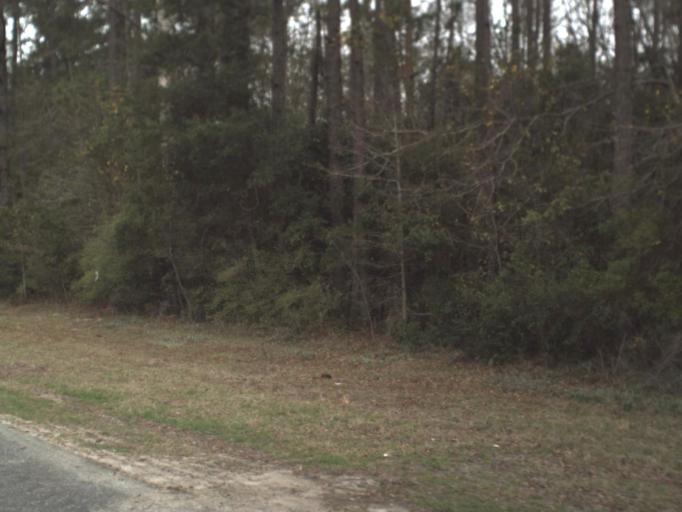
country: US
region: Florida
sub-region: Jefferson County
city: Monticello
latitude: 30.4947
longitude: -83.7387
